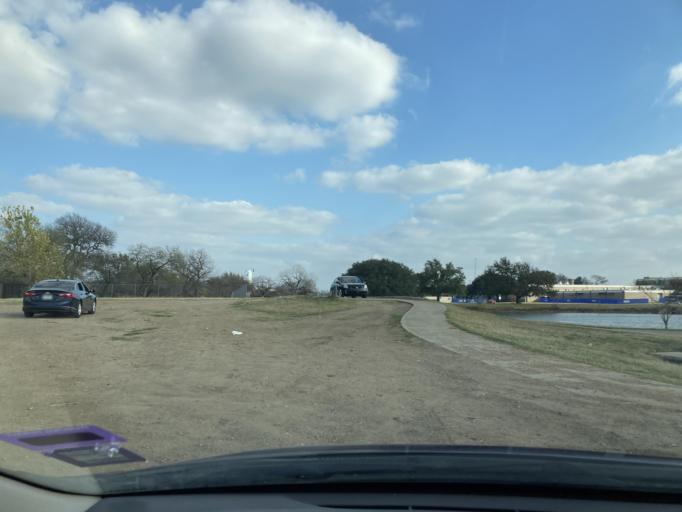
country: US
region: Texas
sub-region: Dallas County
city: Cockrell Hill
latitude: 32.7833
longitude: -96.8617
